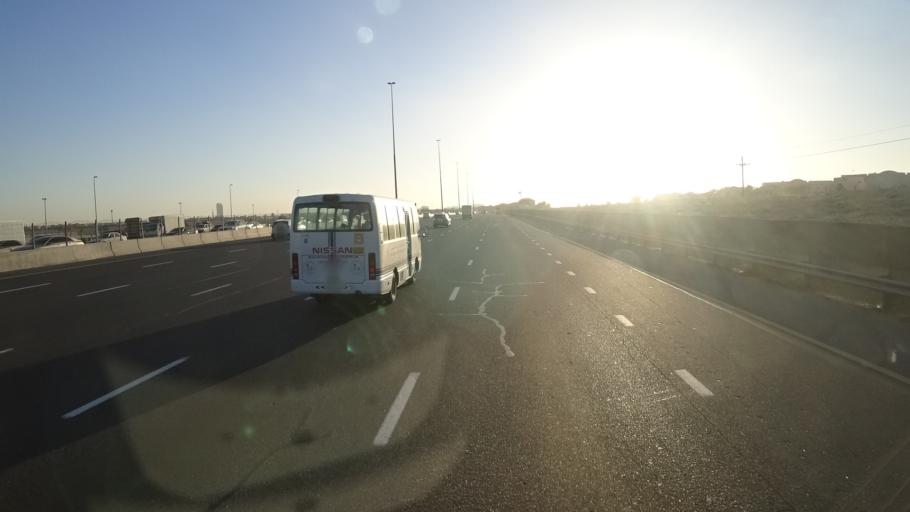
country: AE
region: Dubai
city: Dubai
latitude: 25.1138
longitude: 55.3523
